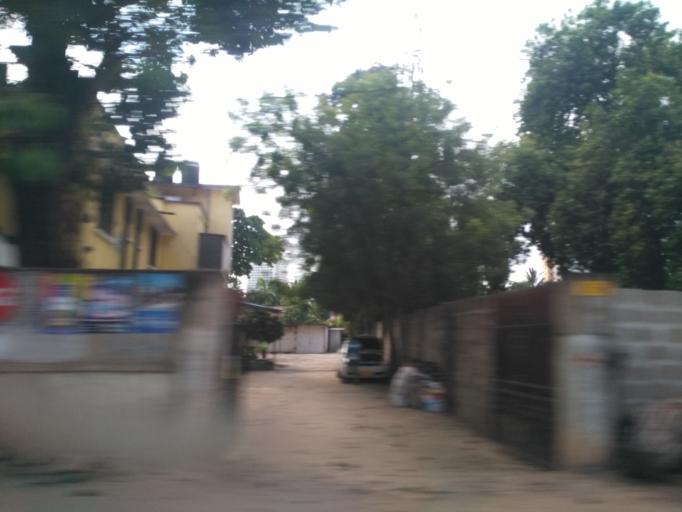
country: TZ
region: Dar es Salaam
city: Dar es Salaam
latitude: -6.8077
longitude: 39.2800
